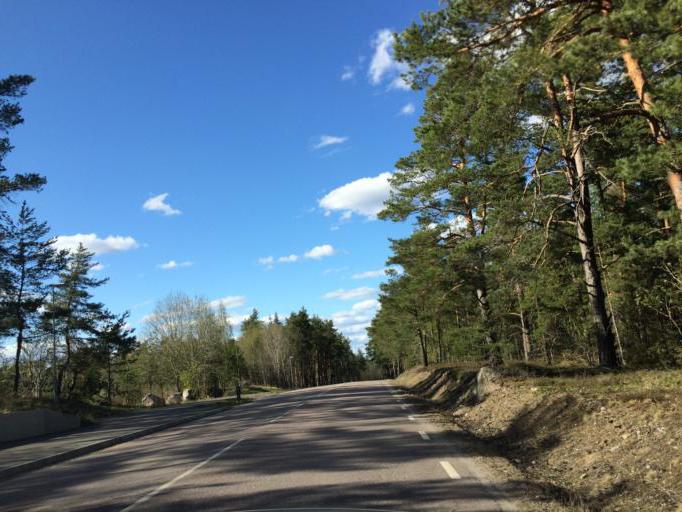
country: SE
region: Soedermanland
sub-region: Eskilstuna Kommun
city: Hallbybrunn
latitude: 59.3579
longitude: 16.4357
